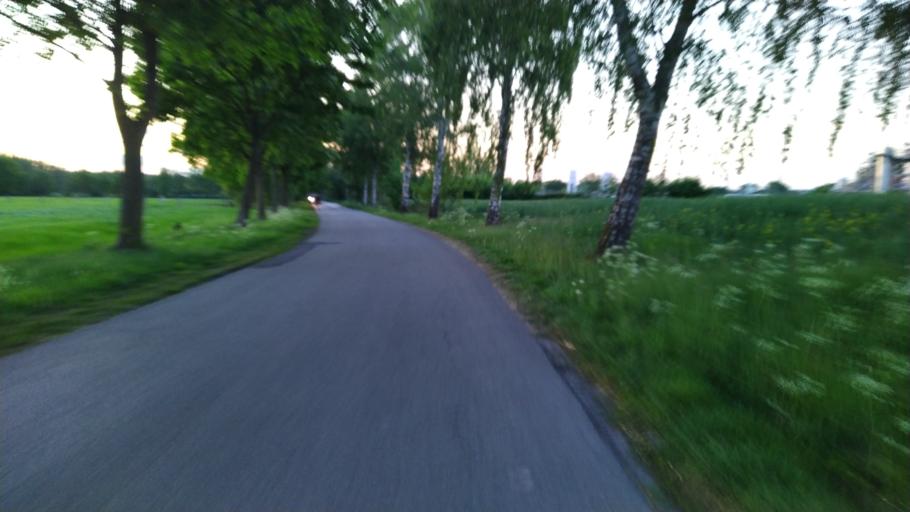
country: DE
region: Lower Saxony
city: Bargstedt
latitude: 53.4747
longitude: 9.4703
